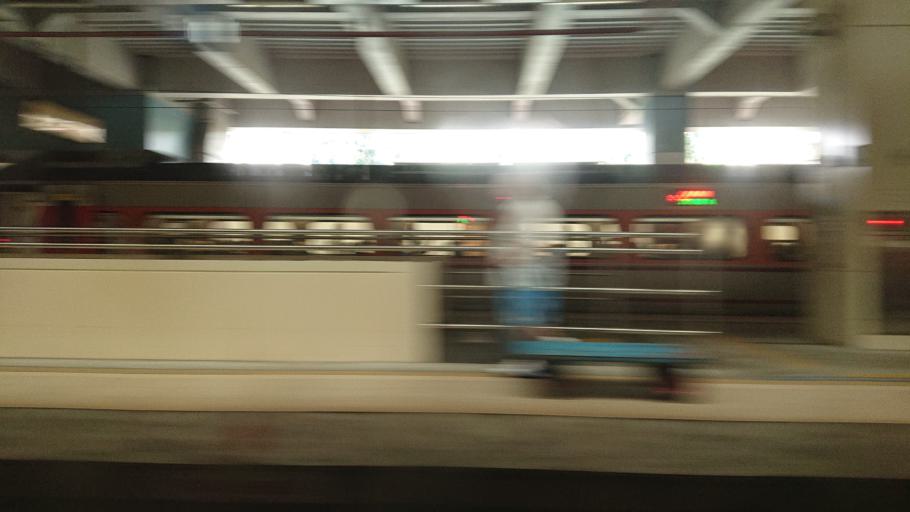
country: TW
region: Taiwan
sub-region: Keelung
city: Keelung
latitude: 25.0931
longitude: 121.7143
